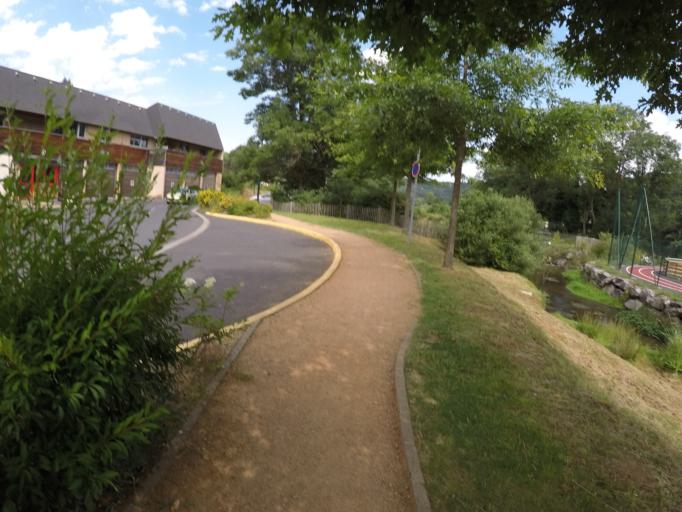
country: FR
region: Auvergne
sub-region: Departement du Puy-de-Dome
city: Aydat
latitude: 45.6611
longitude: 2.9753
